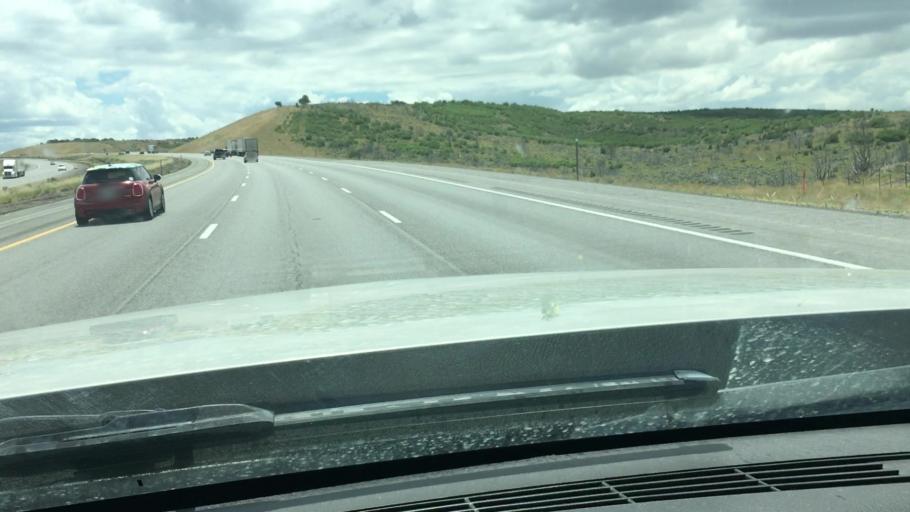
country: US
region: Utah
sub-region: Beaver County
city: Beaver
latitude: 38.4865
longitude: -112.6183
